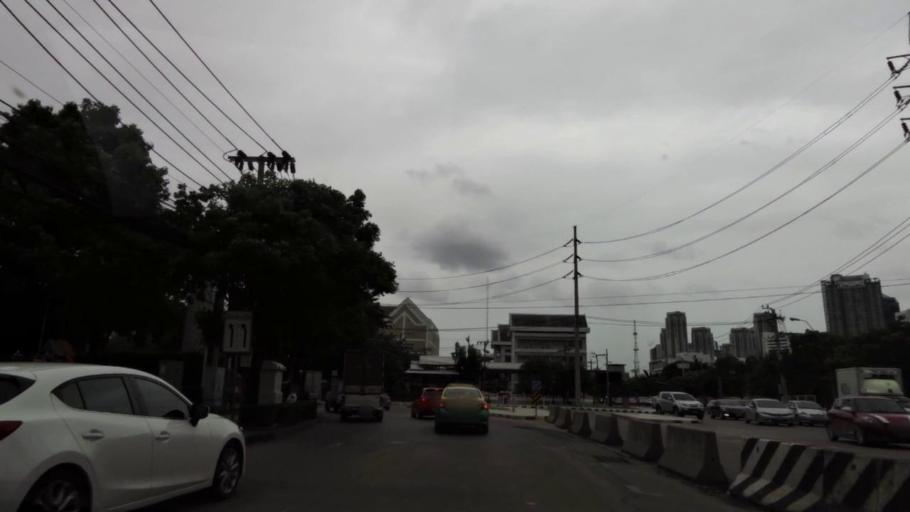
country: TH
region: Bangkok
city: Huai Khwang
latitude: 13.7685
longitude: 100.5733
